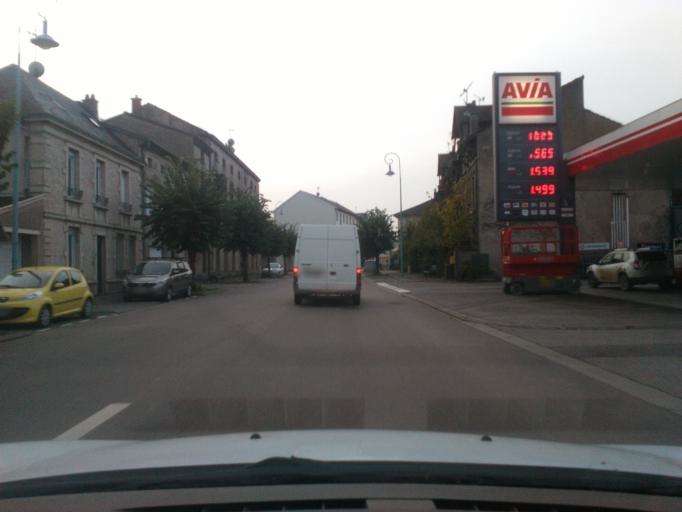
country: FR
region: Lorraine
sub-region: Departement des Vosges
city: Mirecourt
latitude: 48.3074
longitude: 6.1337
